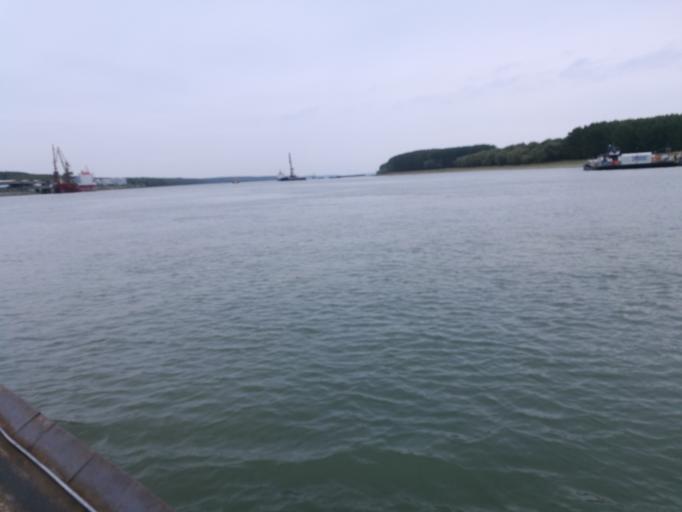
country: RO
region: Braila
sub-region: Municipiul Braila
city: Braila
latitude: 45.2873
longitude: 27.9953
